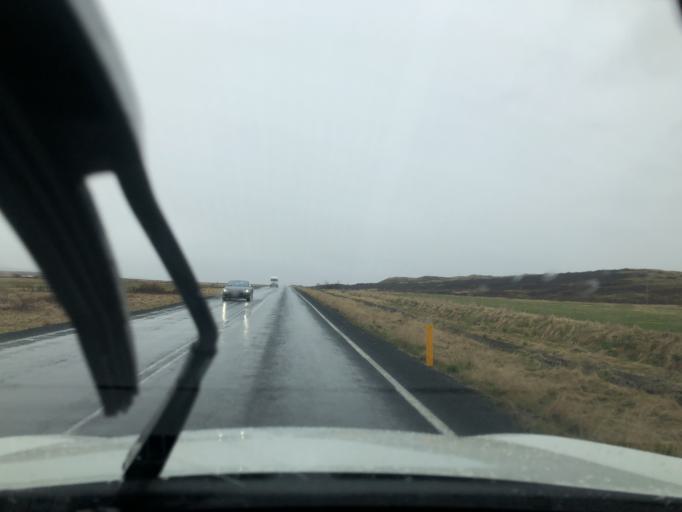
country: IS
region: South
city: Selfoss
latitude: 64.2986
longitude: -20.3323
